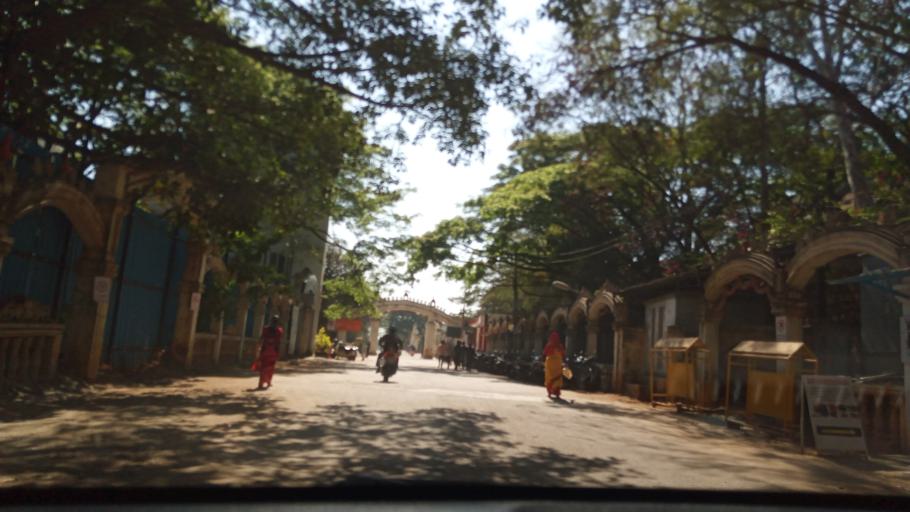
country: IN
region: Karnataka
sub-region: Bangalore Urban
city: Bangalore
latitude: 13.0300
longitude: 77.5636
